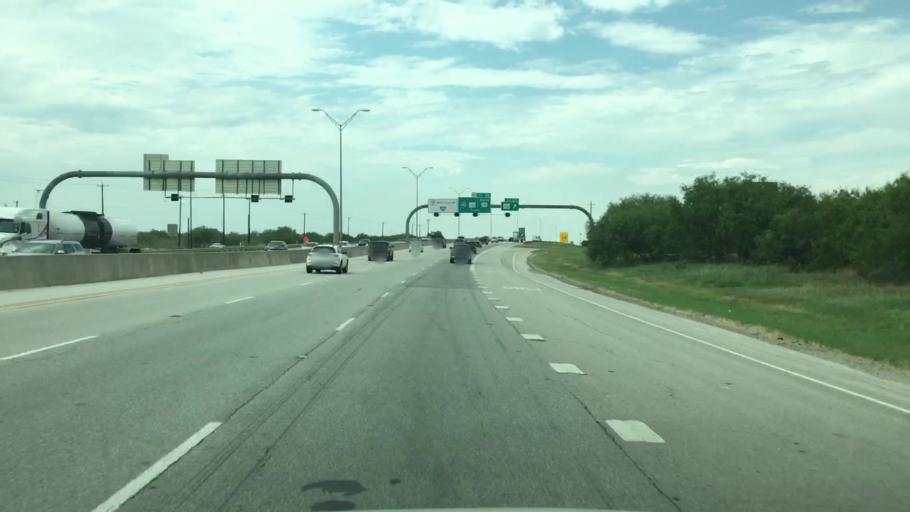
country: US
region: Texas
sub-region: Bexar County
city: Elmendorf
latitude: 29.3123
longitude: -98.4040
